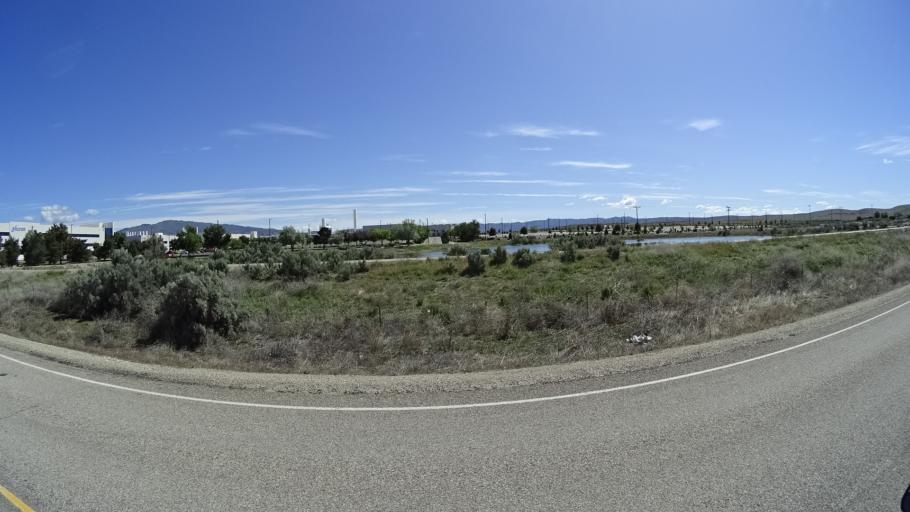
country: US
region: Idaho
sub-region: Ada County
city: Boise
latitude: 43.5212
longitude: -116.1470
